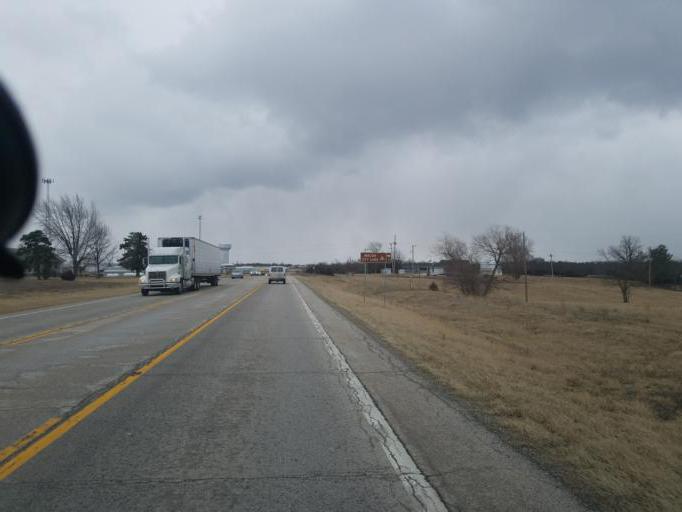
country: US
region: Missouri
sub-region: Macon County
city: Macon
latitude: 39.7681
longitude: -92.4708
